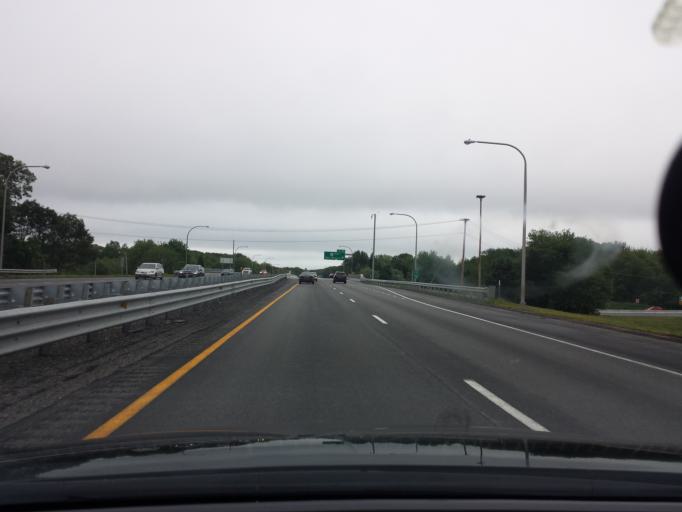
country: US
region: Rhode Island
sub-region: Kent County
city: West Warwick
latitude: 41.6665
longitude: -71.5009
